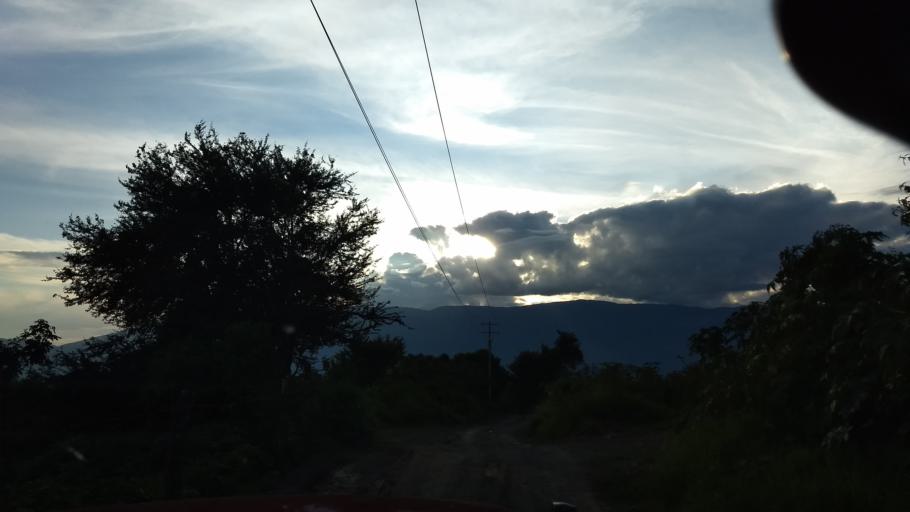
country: MX
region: Jalisco
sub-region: San Gabriel
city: Alista
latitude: 19.5060
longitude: -103.7570
